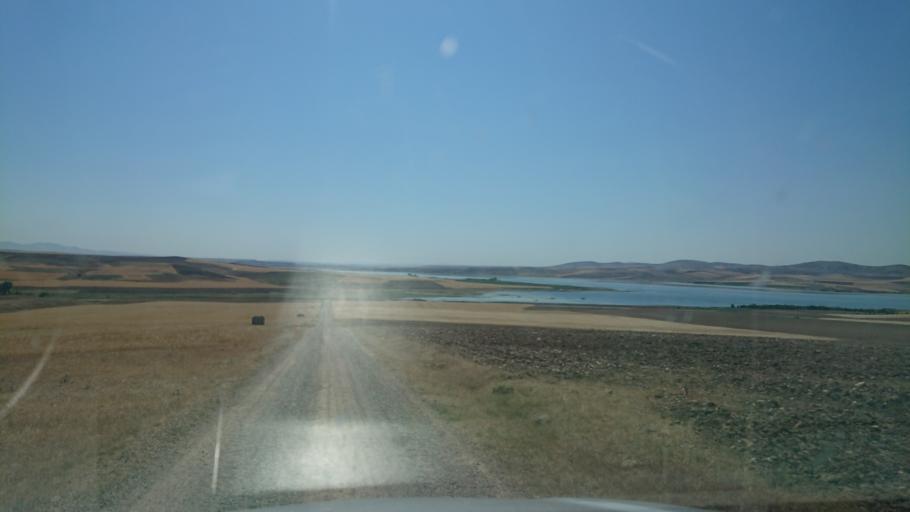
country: TR
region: Aksaray
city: Sariyahsi
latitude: 39.0560
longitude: 33.8909
